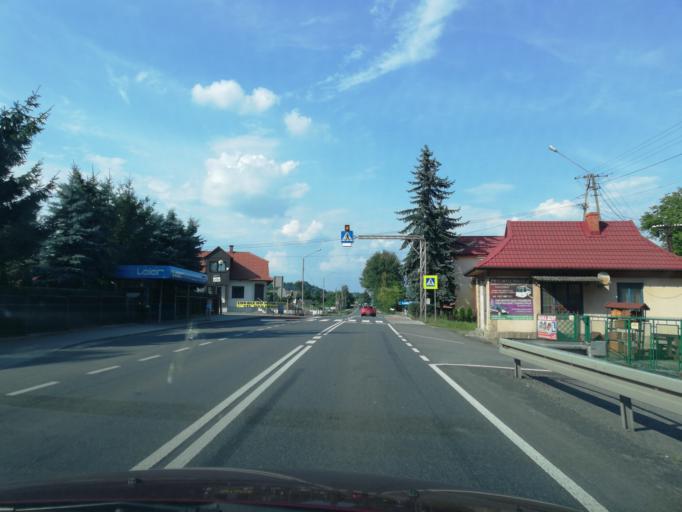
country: PL
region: Lesser Poland Voivodeship
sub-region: Powiat brzeski
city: Czchow
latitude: 49.8339
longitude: 20.6790
